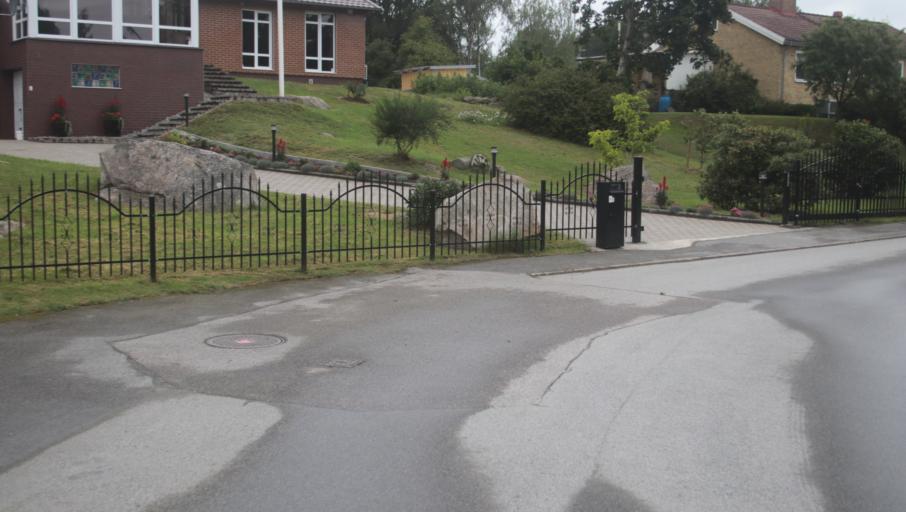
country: SE
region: Blekinge
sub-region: Karlshamns Kommun
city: Svangsta
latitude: 56.2642
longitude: 14.7729
